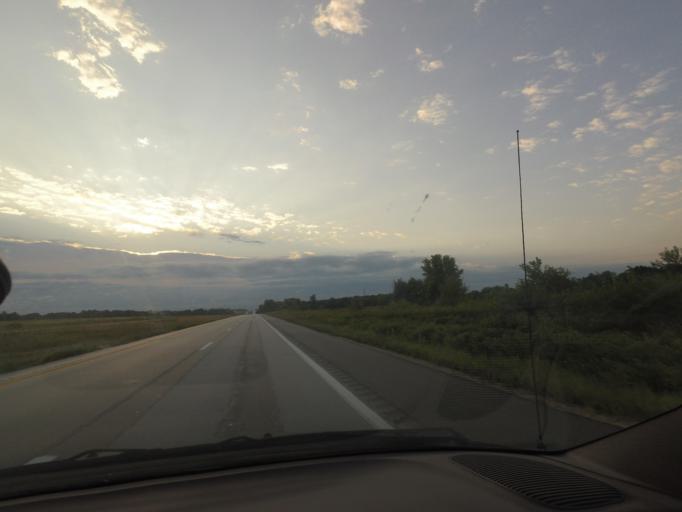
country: US
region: Missouri
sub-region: Shelby County
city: Shelbina
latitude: 39.7256
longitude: -92.1767
